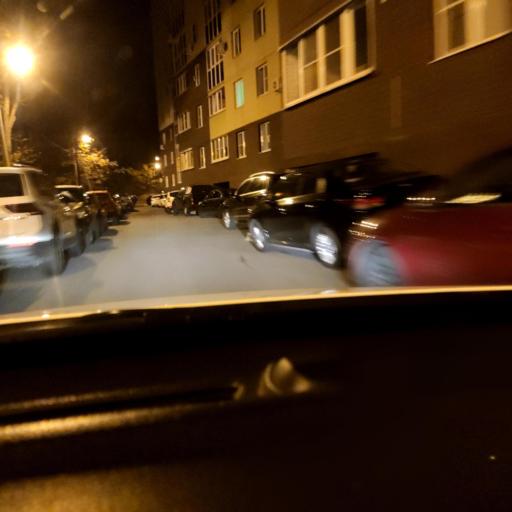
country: RU
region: Voronezj
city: Voronezh
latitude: 51.6977
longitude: 39.2226
